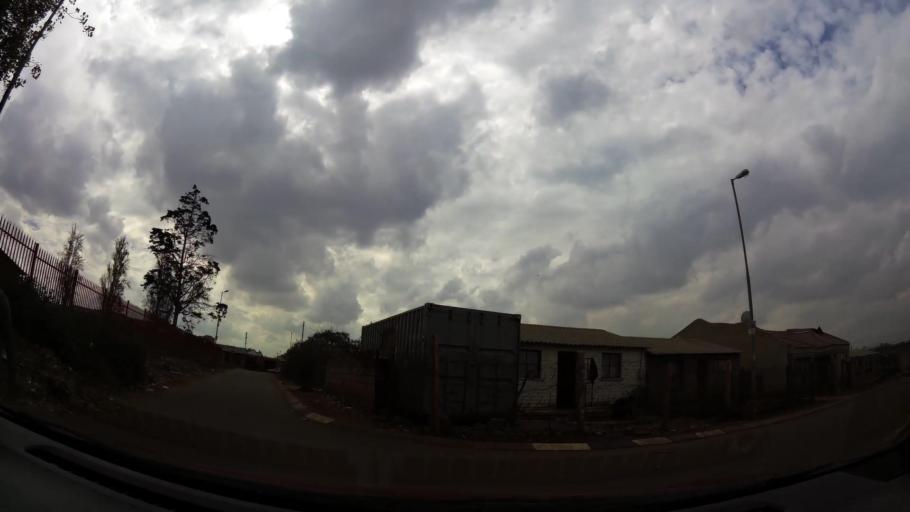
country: ZA
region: Gauteng
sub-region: City of Johannesburg Metropolitan Municipality
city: Soweto
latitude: -26.2571
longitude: 27.8342
